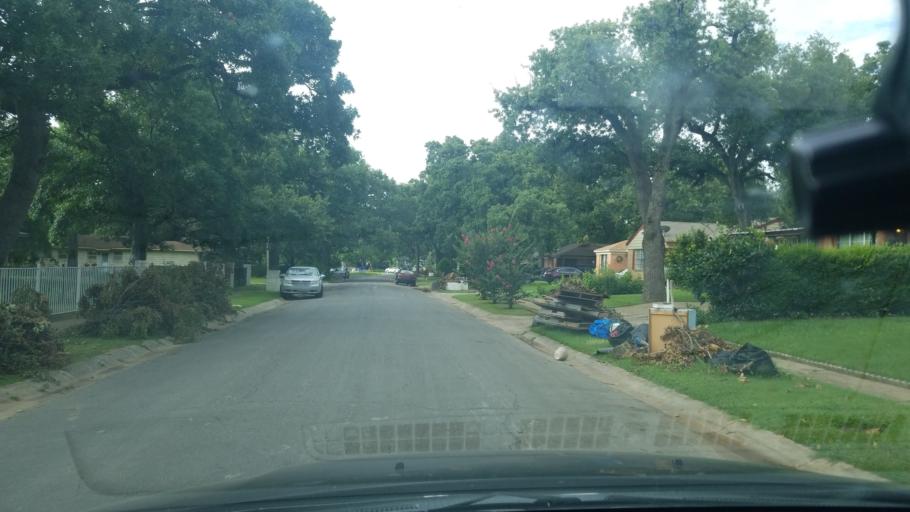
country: US
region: Texas
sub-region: Dallas County
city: Balch Springs
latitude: 32.7374
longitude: -96.6733
